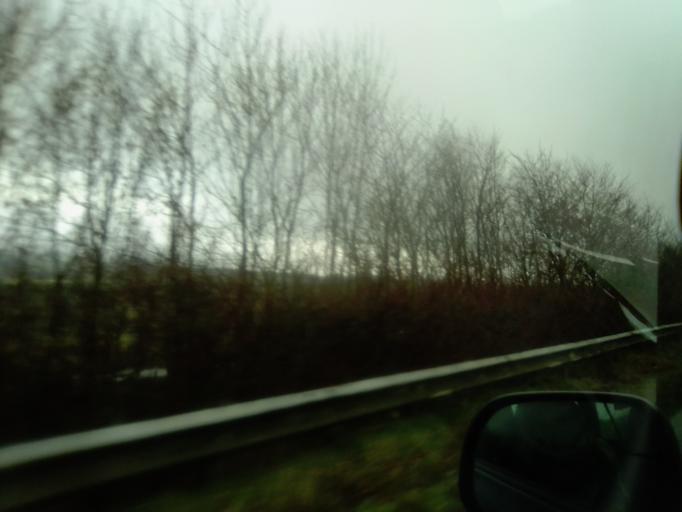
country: GB
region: Northern Ireland
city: Newtownstewart
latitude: 54.7169
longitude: -7.3648
